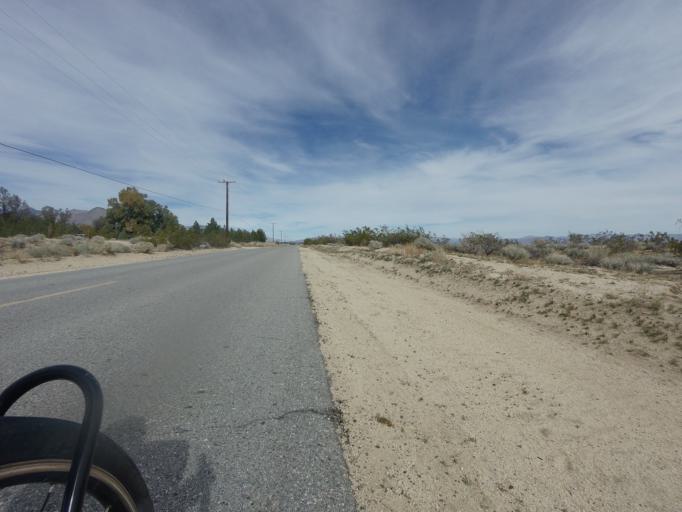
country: US
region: California
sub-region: Kern County
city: Inyokern
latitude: 35.7265
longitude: -117.8359
